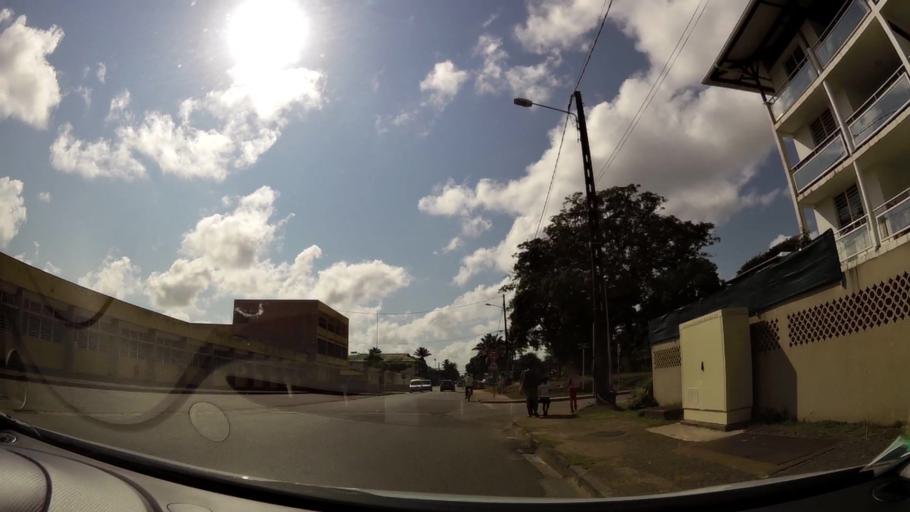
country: GF
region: Guyane
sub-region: Guyane
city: Cayenne
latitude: 4.9344
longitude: -52.3178
